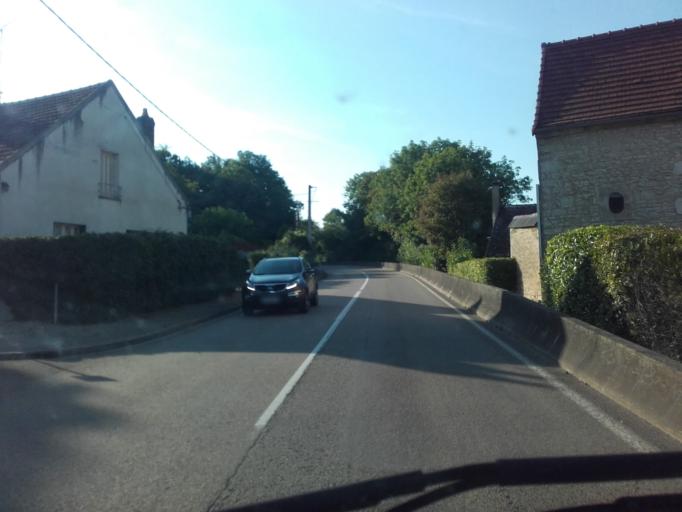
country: FR
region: Bourgogne
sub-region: Departement de l'Yonne
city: Chablis
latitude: 47.8224
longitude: 3.7742
